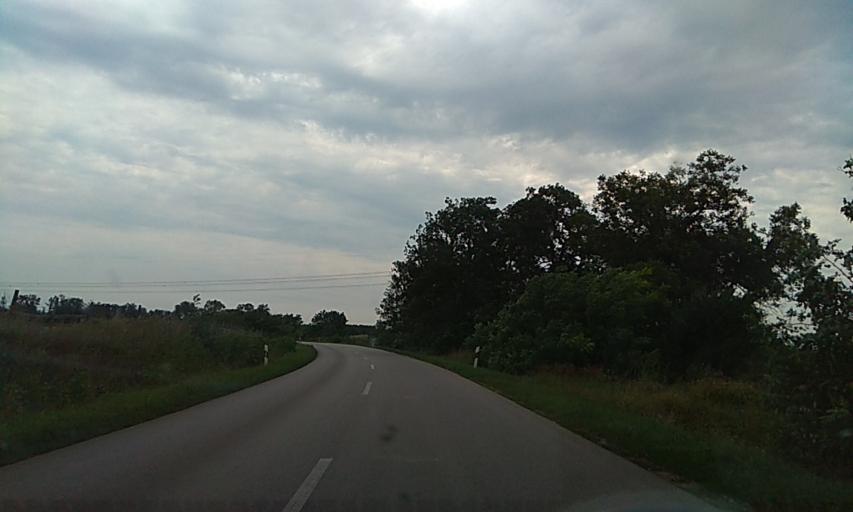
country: HU
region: Szabolcs-Szatmar-Bereg
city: Buj
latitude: 48.0643
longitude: 21.6471
